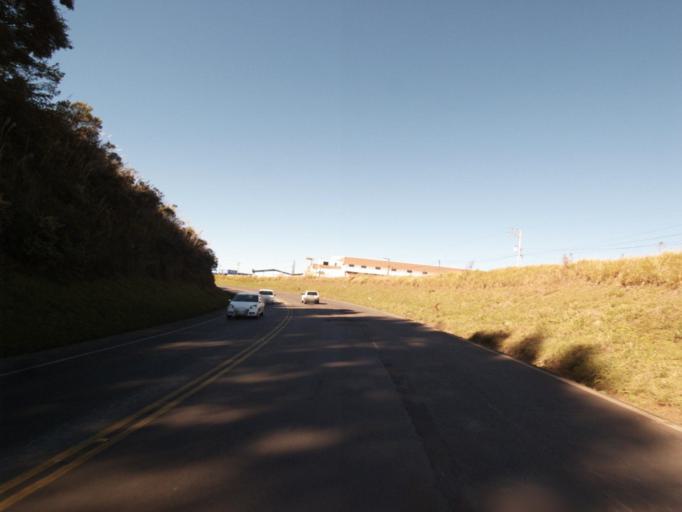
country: BR
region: Santa Catarina
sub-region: Chapeco
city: Chapeco
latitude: -26.9661
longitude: -52.5560
